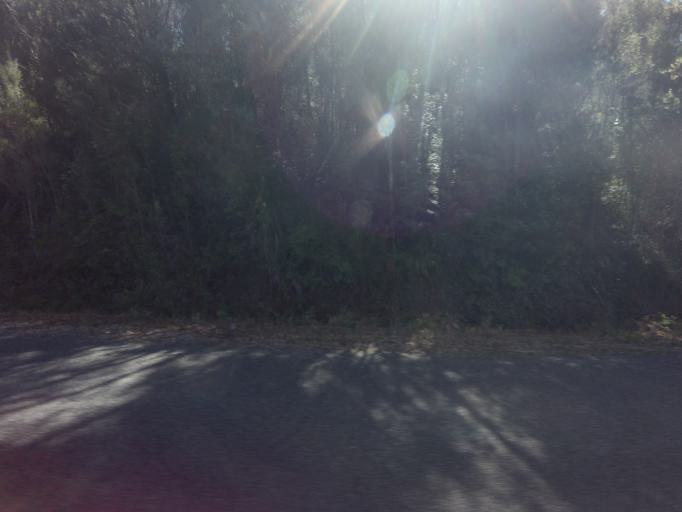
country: AU
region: Tasmania
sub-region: West Coast
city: Queenstown
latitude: -42.7754
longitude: 146.0382
